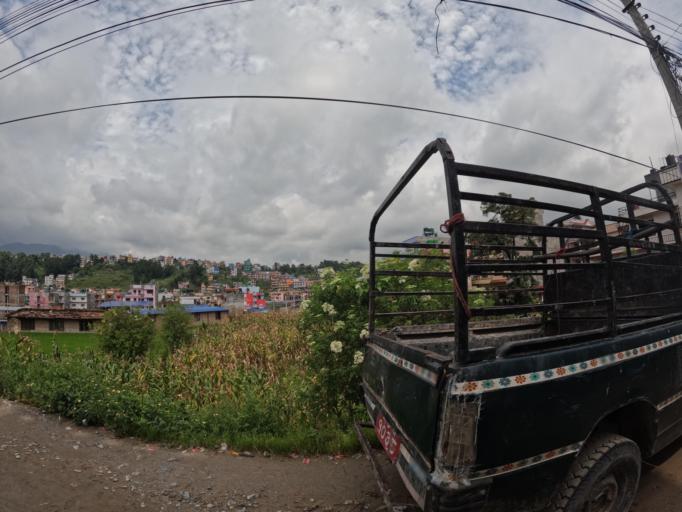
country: NP
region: Central Region
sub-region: Bagmati Zone
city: Kathmandu
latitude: 27.7557
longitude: 85.3181
